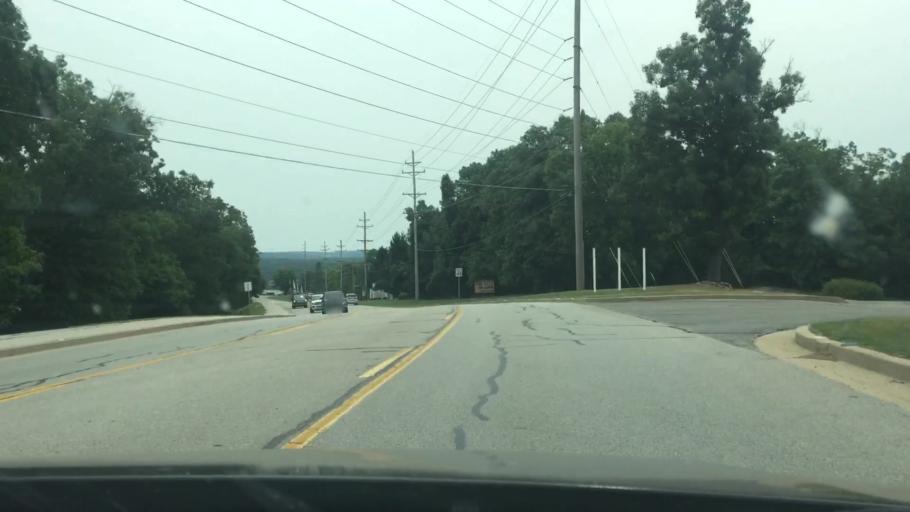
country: US
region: Missouri
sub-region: Miller County
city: Lake Ozark
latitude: 38.1938
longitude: -92.6732
